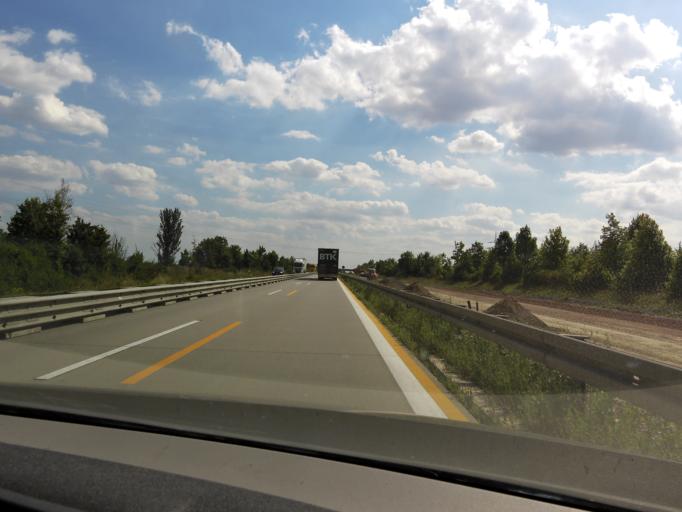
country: DE
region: Saxony-Anhalt
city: Plotzkau
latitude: 51.7697
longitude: 11.6715
